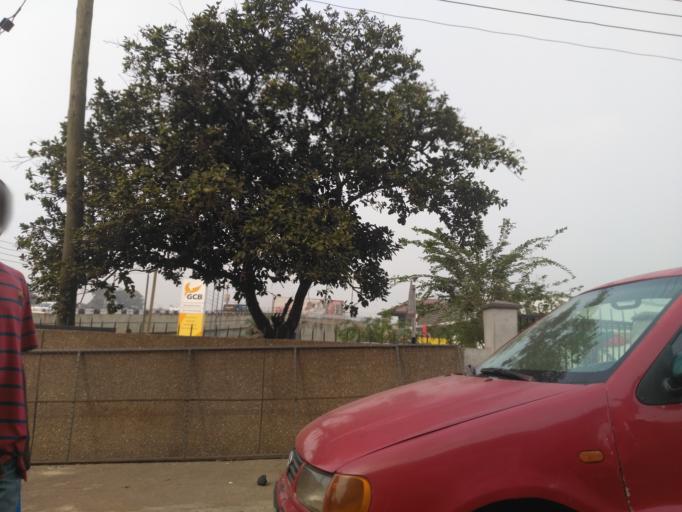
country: GH
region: Ashanti
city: Kumasi
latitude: 6.6895
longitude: -1.6159
